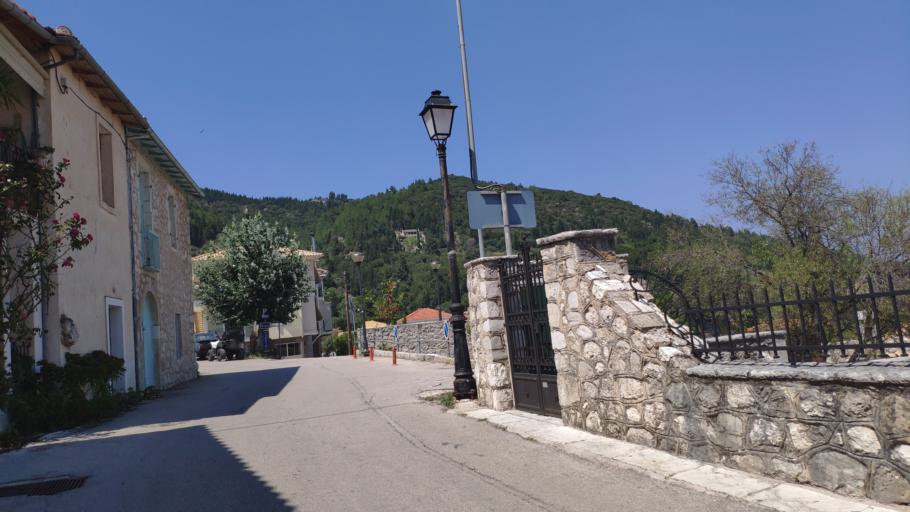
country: GR
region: Ionian Islands
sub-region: Lefkada
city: Nidri
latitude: 38.7602
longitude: 20.6480
